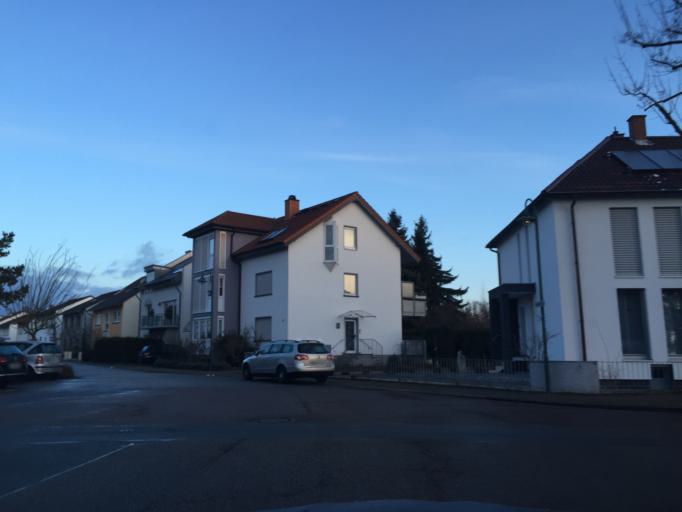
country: DE
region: Baden-Wuerttemberg
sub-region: Karlsruhe Region
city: Schwetzingen
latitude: 49.3873
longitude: 8.5863
